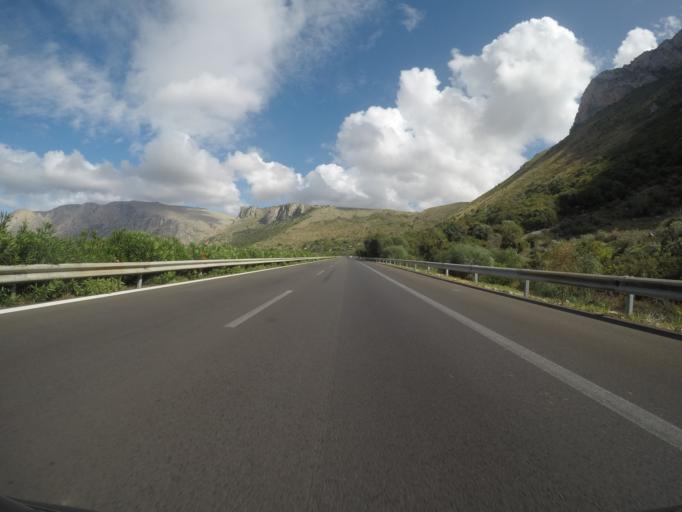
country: IT
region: Sicily
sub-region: Palermo
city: Terrasini
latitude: 38.1356
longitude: 13.0877
